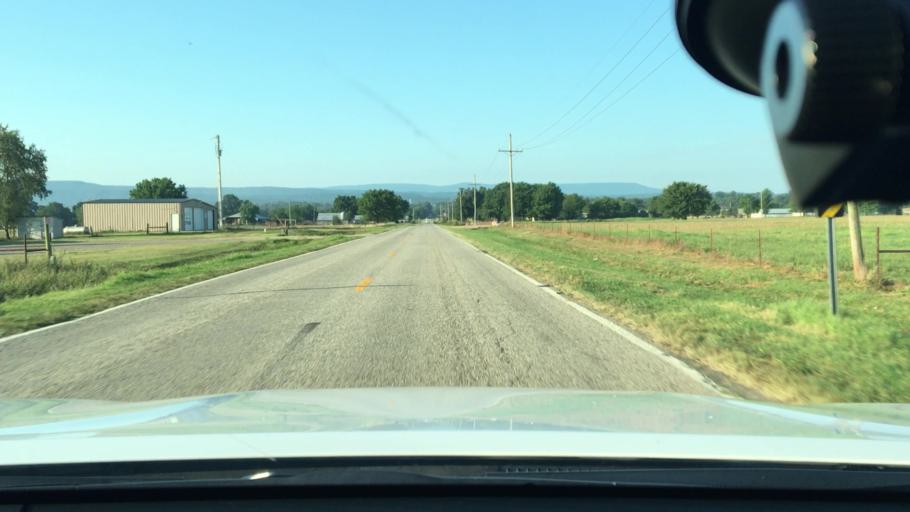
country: US
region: Arkansas
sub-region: Logan County
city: Paris
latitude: 35.3301
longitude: -93.6320
